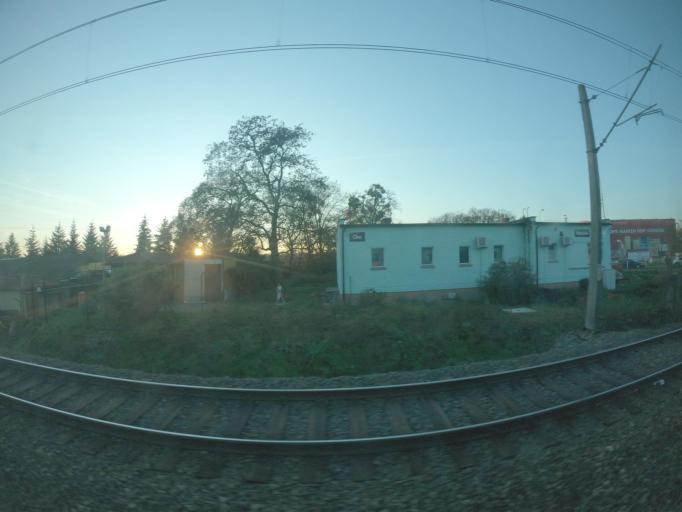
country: PL
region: Lubusz
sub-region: Powiat gorzowski
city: Kostrzyn nad Odra
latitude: 52.5807
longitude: 14.6427
